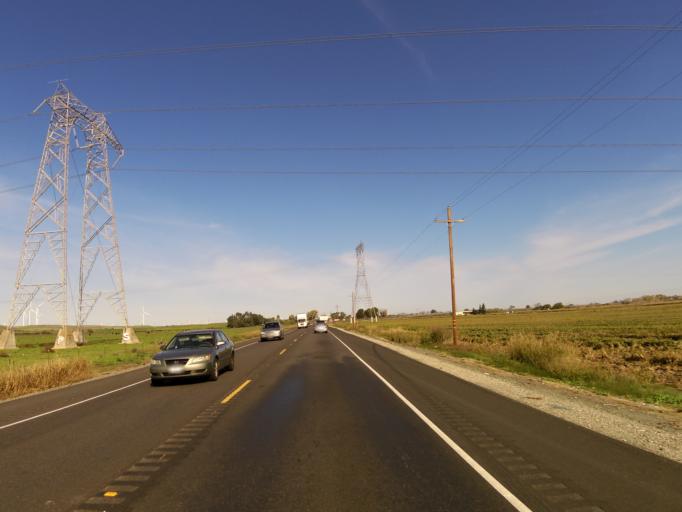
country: US
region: California
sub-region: Contra Costa County
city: Oakley
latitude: 38.0730
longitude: -121.7344
